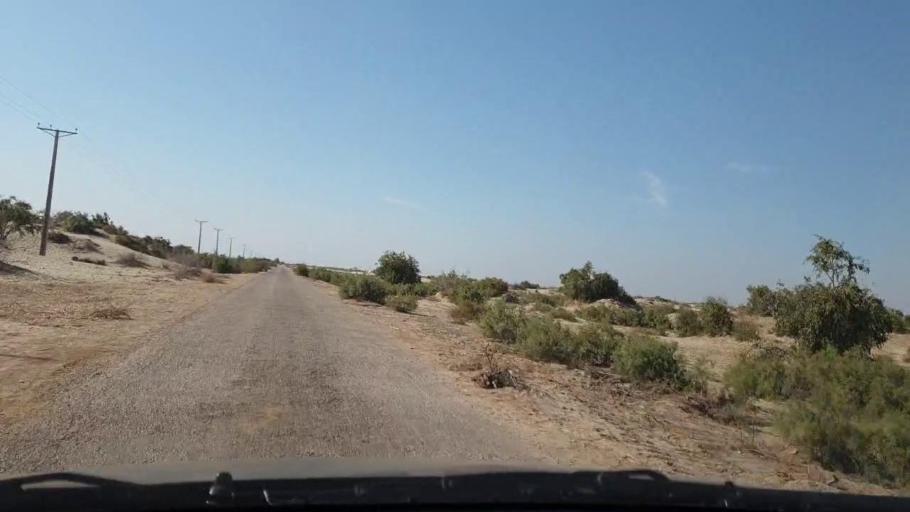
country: PK
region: Sindh
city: Khadro
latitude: 26.2684
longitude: 68.7957
